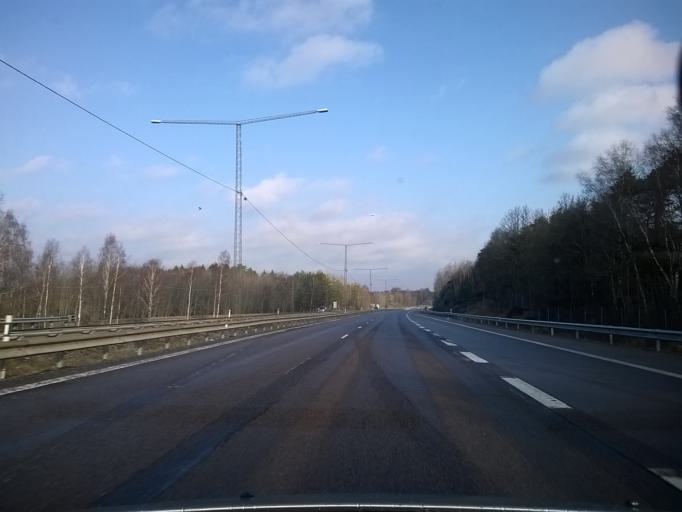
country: SE
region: Vaestra Goetaland
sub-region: Kungalvs Kommun
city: Kode
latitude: 57.9467
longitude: 11.8550
